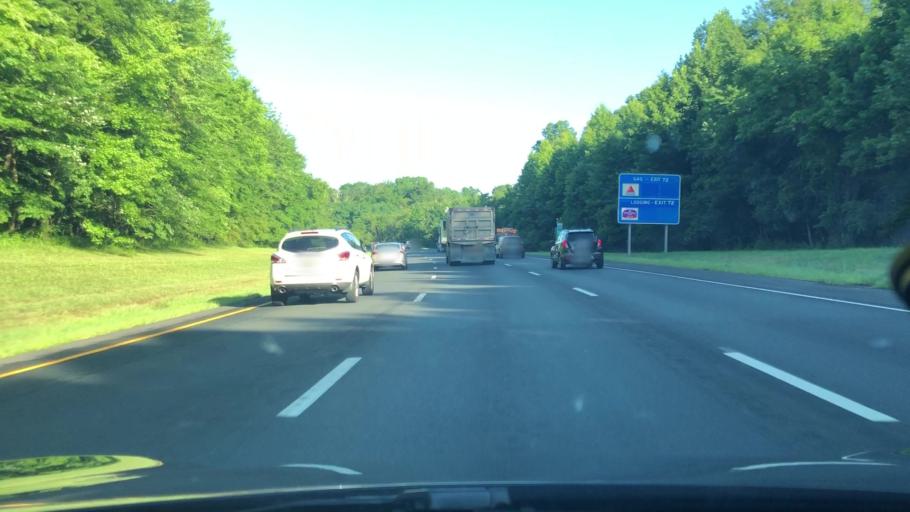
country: US
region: New Jersey
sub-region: Mercer County
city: Lawrenceville
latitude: 40.2922
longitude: -74.7678
